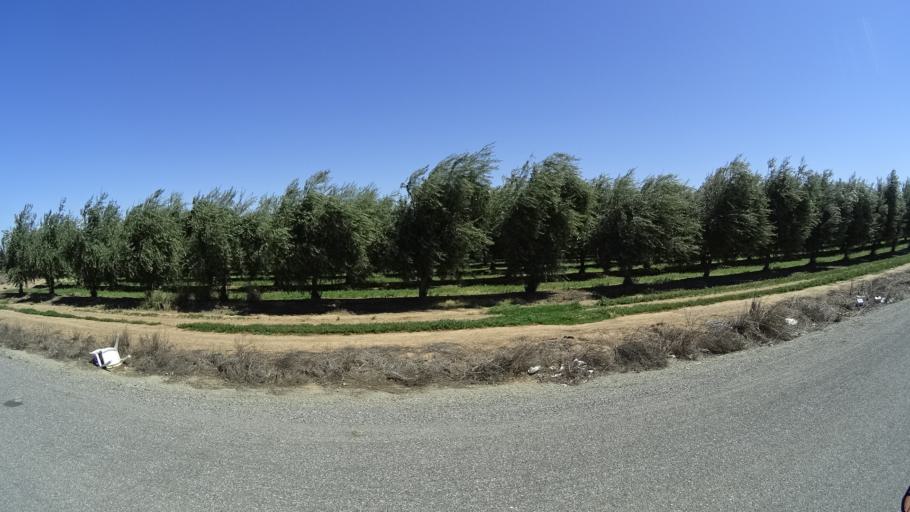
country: US
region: California
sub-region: Glenn County
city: Orland
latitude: 39.7905
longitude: -122.1784
